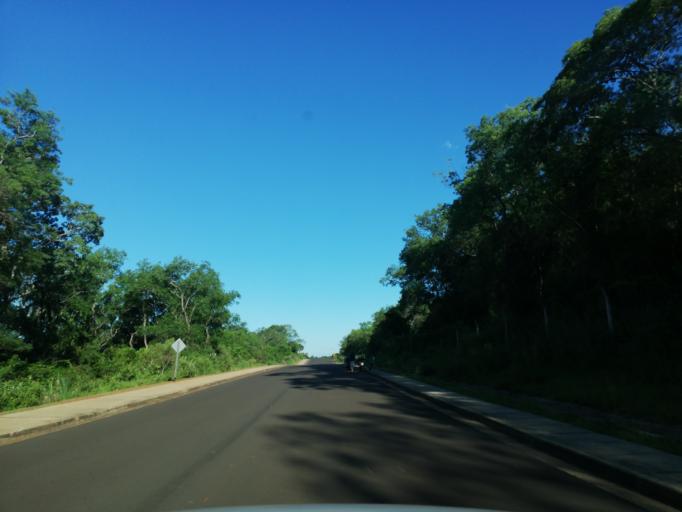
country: AR
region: Misiones
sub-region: Departamento de Candelaria
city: Candelaria
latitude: -27.4500
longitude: -55.7707
